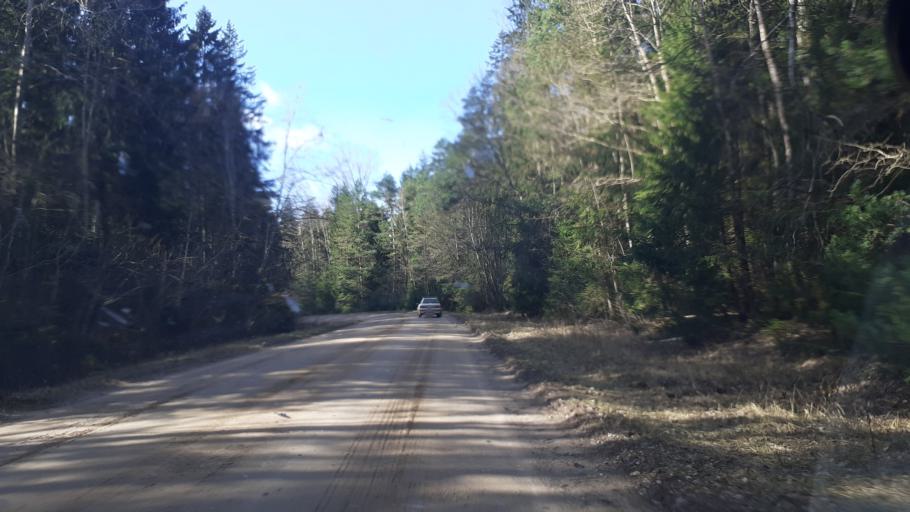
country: LV
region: Kuldigas Rajons
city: Kuldiga
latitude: 56.9105
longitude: 22.0797
